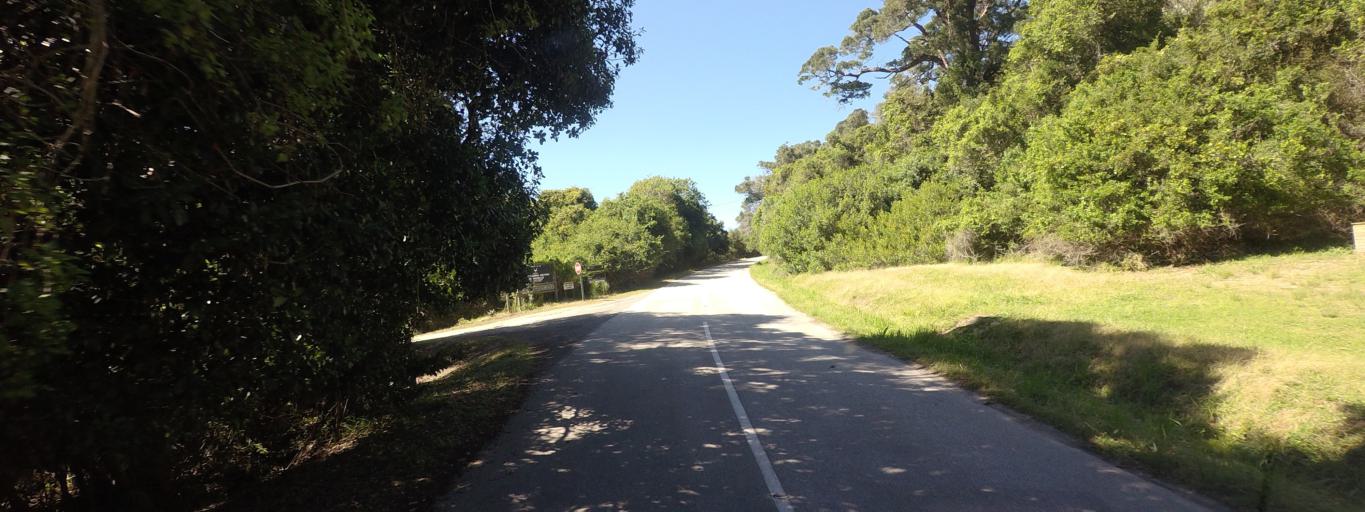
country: ZA
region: Western Cape
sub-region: Eden District Municipality
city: Plettenberg Bay
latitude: -33.9705
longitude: 23.5617
